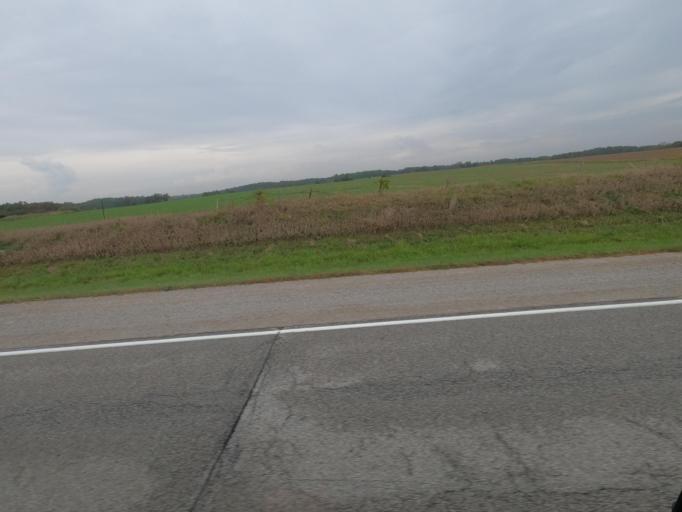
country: US
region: Iowa
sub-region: Van Buren County
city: Keosauqua
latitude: 40.8433
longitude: -92.0182
